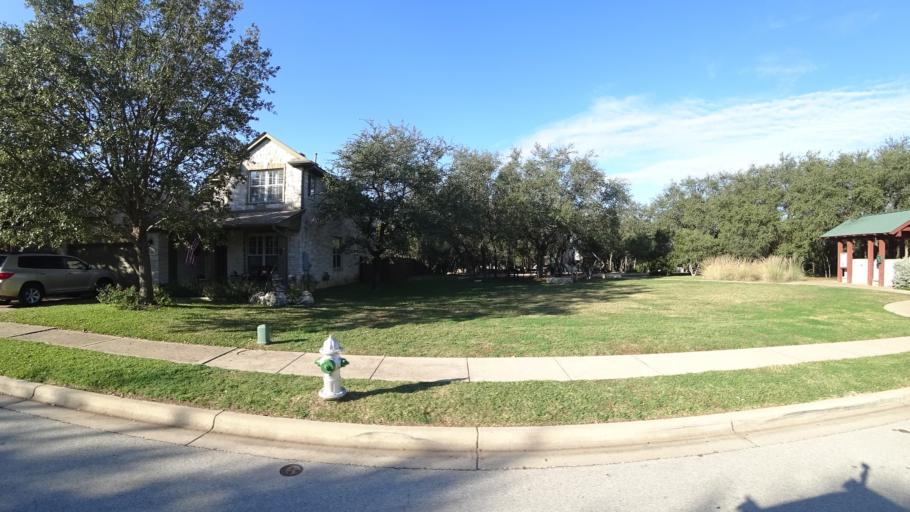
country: US
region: Texas
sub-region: Travis County
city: Hudson Bend
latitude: 30.3704
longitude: -97.8982
